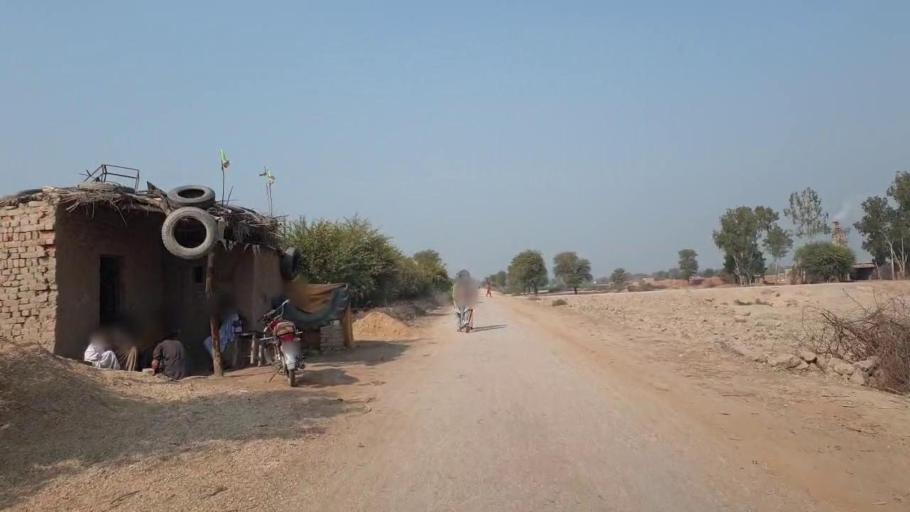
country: PK
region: Sindh
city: Hala
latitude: 25.8572
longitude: 68.4619
